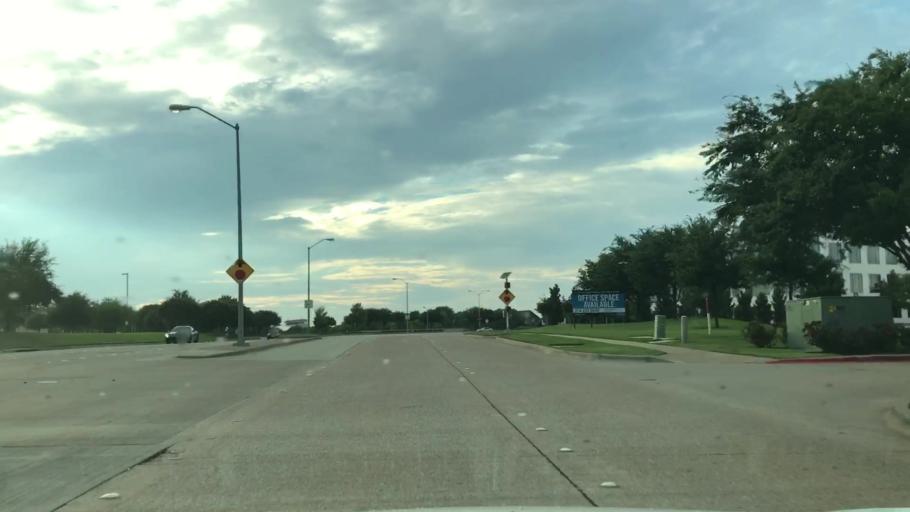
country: US
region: Texas
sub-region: Dallas County
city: Addison
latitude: 33.0171
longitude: -96.8326
